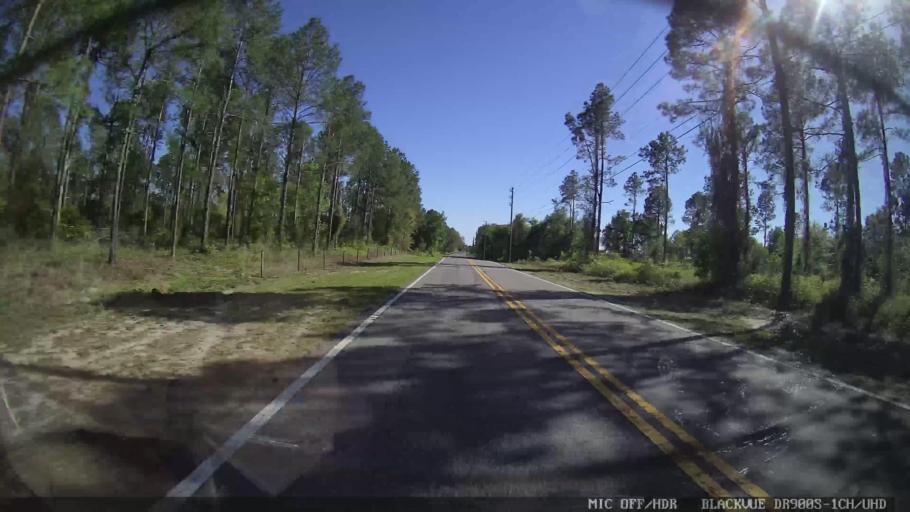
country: US
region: Florida
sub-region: Pasco County
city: Shady Hills
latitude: 28.3585
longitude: -82.5425
